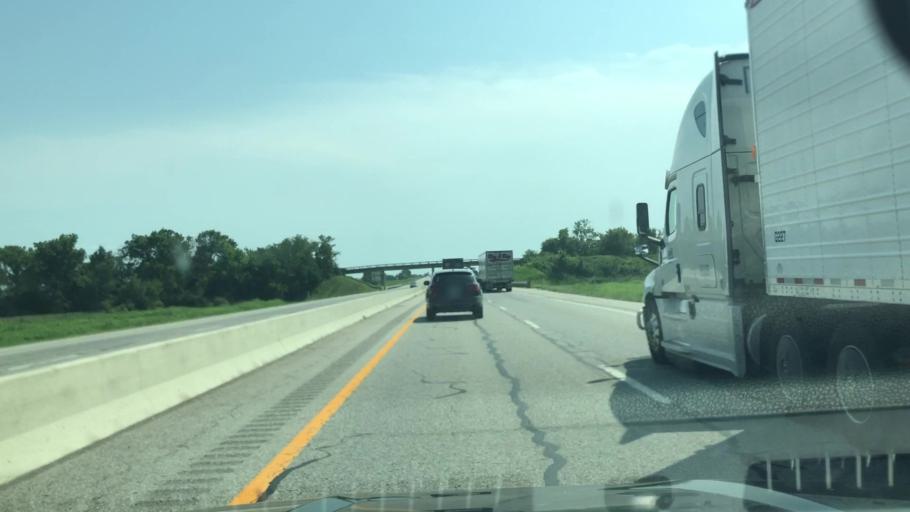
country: US
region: Oklahoma
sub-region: Ottawa County
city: Miami
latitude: 36.8319
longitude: -94.8659
